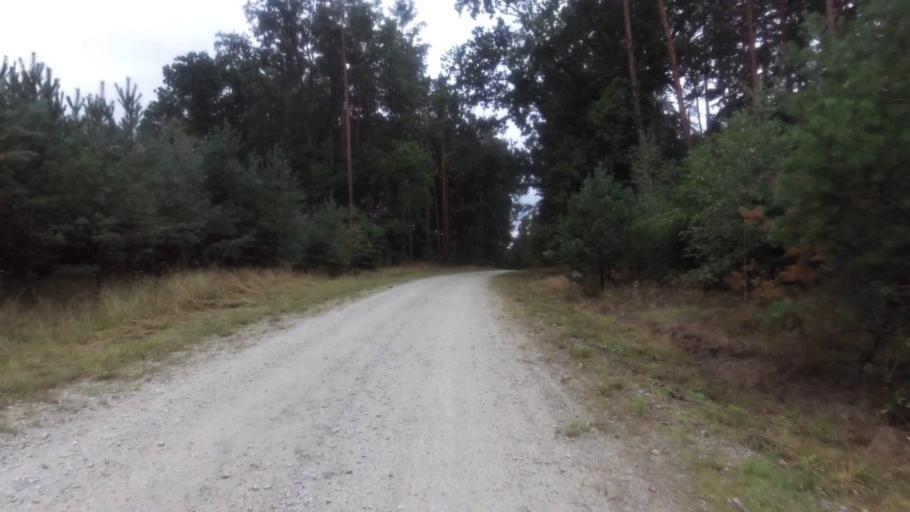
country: PL
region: Lubusz
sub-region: Powiat gorzowski
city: Kostrzyn nad Odra
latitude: 52.6307
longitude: 14.6489
